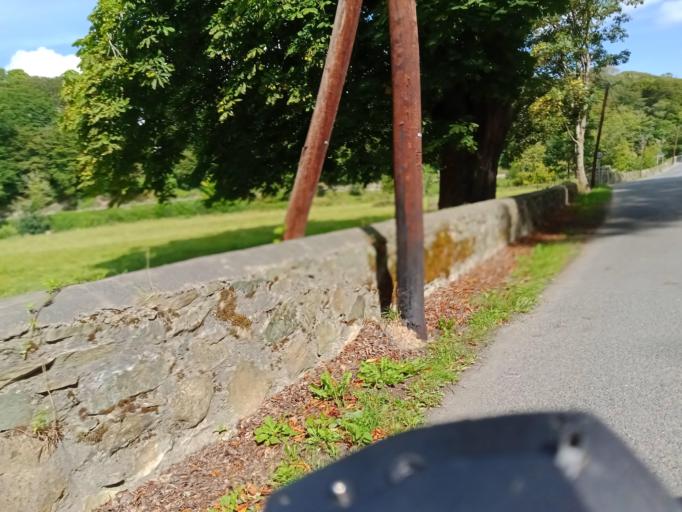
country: IE
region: Munster
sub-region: Waterford
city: Dungarvan
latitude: 52.1248
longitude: -7.4636
